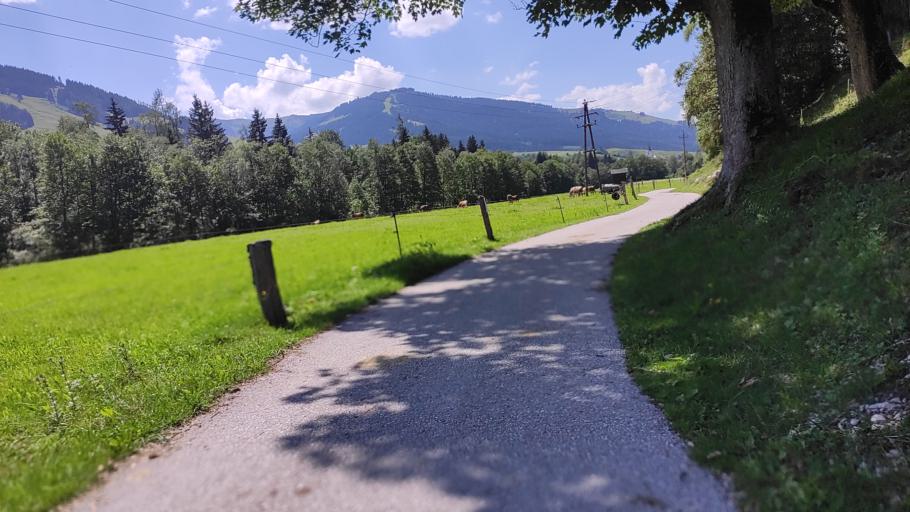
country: AT
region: Salzburg
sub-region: Politischer Bezirk Zell am See
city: Leogang
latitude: 47.4412
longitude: 12.7731
